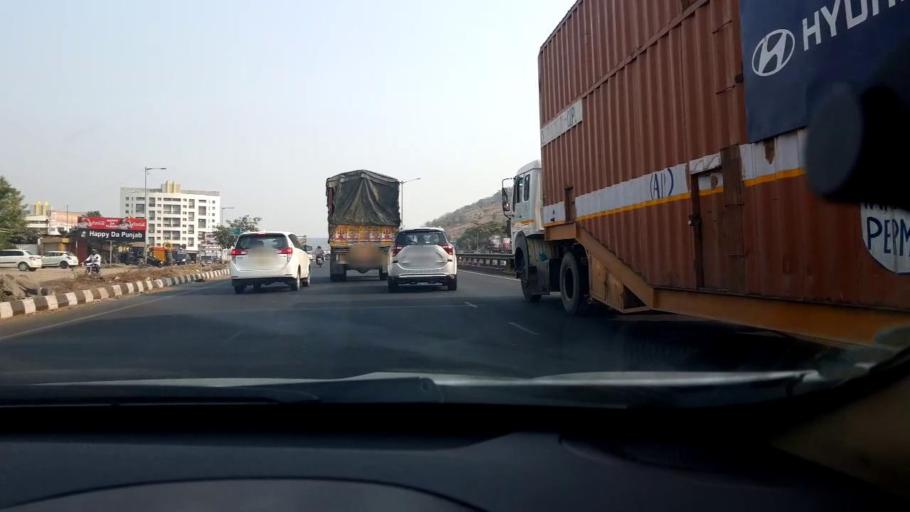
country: IN
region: Maharashtra
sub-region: Pune Division
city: Shivaji Nagar
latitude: 18.5445
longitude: 73.7755
